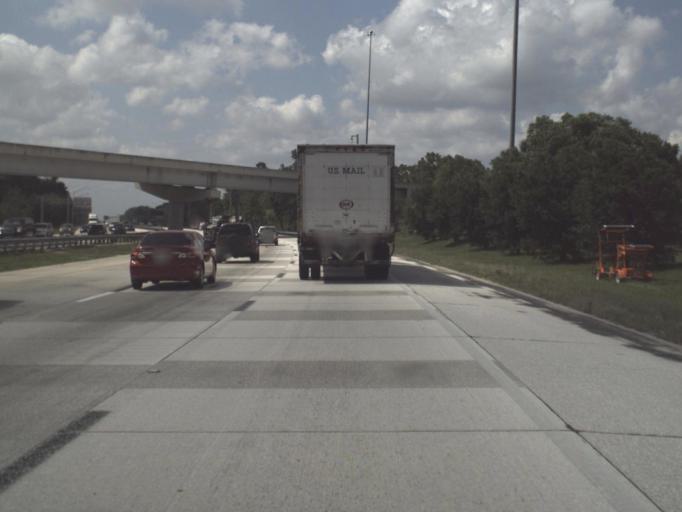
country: US
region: Florida
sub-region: Saint Johns County
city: Fruit Cove
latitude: 30.1977
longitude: -81.5564
